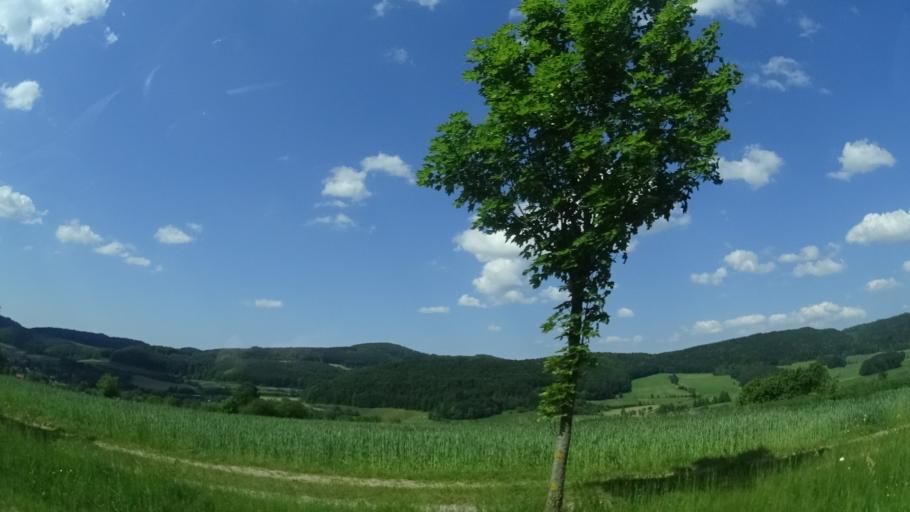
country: DE
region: Hesse
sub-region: Regierungsbezirk Kassel
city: Hofbieber
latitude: 50.6141
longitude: 9.9127
